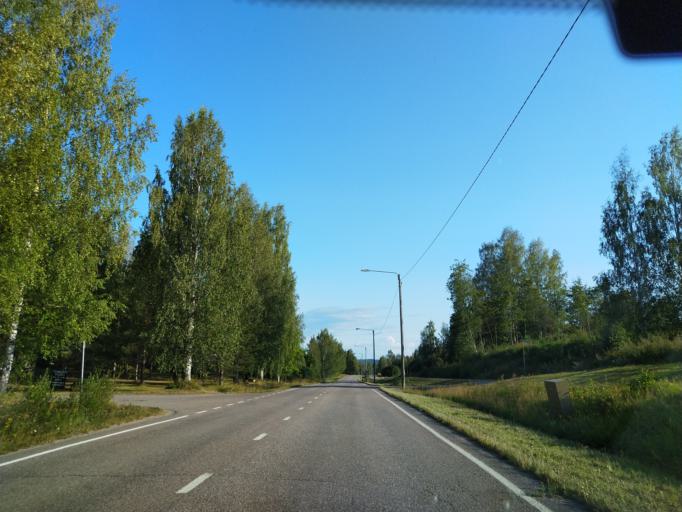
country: FI
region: Central Finland
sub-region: Jaemsae
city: Kuhmoinen
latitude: 61.5784
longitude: 25.1745
